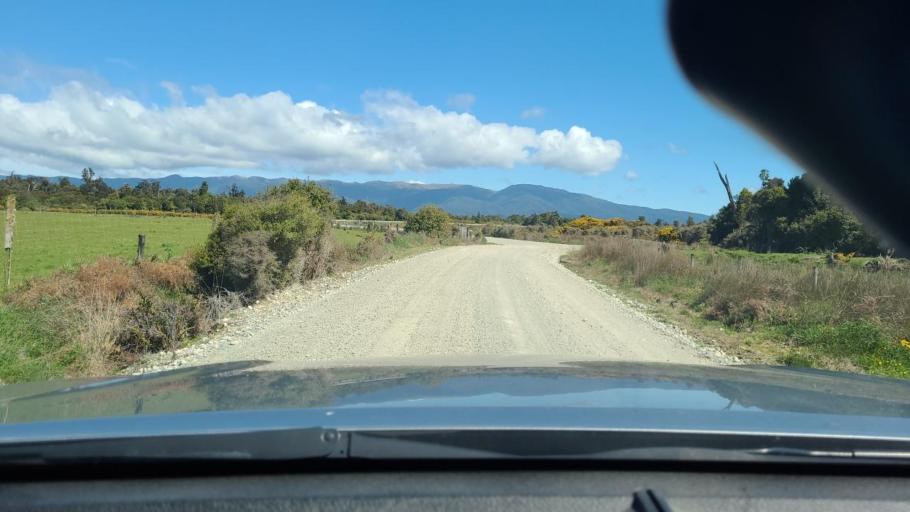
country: NZ
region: Southland
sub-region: Southland District
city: Riverton
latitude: -46.1428
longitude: 167.4851
